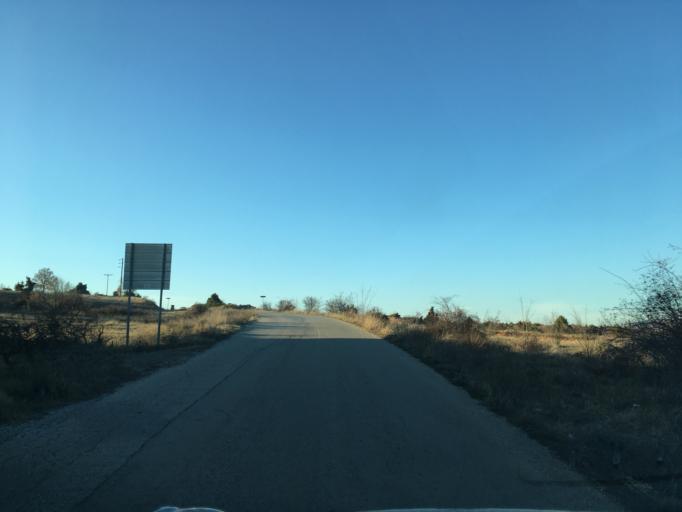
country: GR
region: West Macedonia
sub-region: Nomos Kozanis
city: Kozani
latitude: 40.2676
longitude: 21.7436
